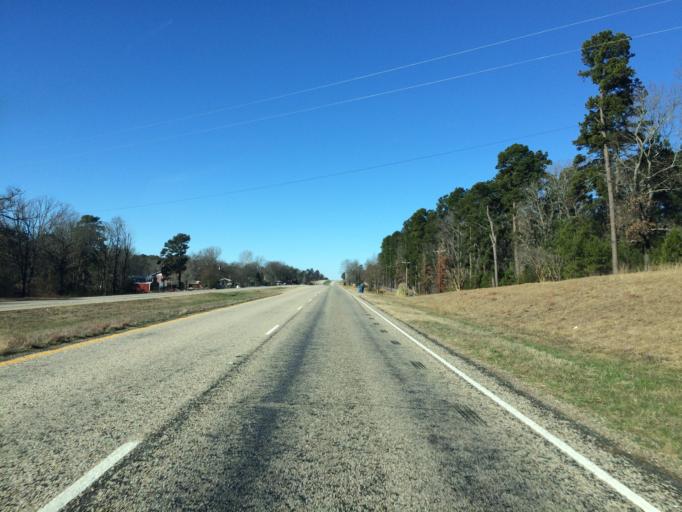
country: US
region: Texas
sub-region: Wood County
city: Mineola
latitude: 32.6505
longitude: -95.4288
